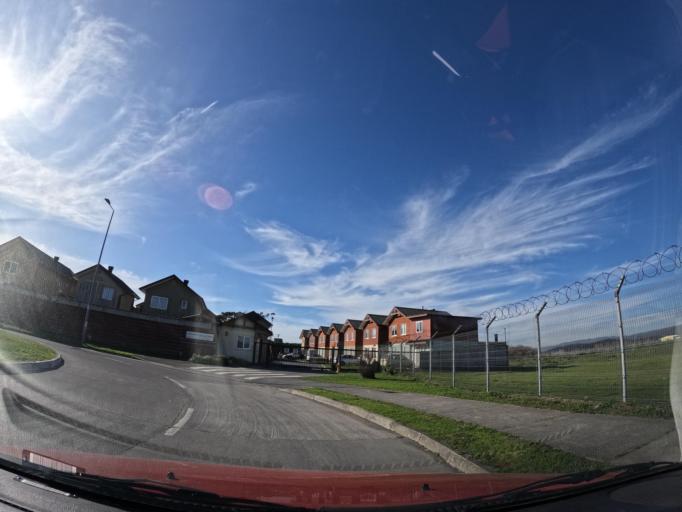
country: CL
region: Biobio
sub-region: Provincia de Concepcion
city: Concepcion
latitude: -36.7695
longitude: -73.0652
